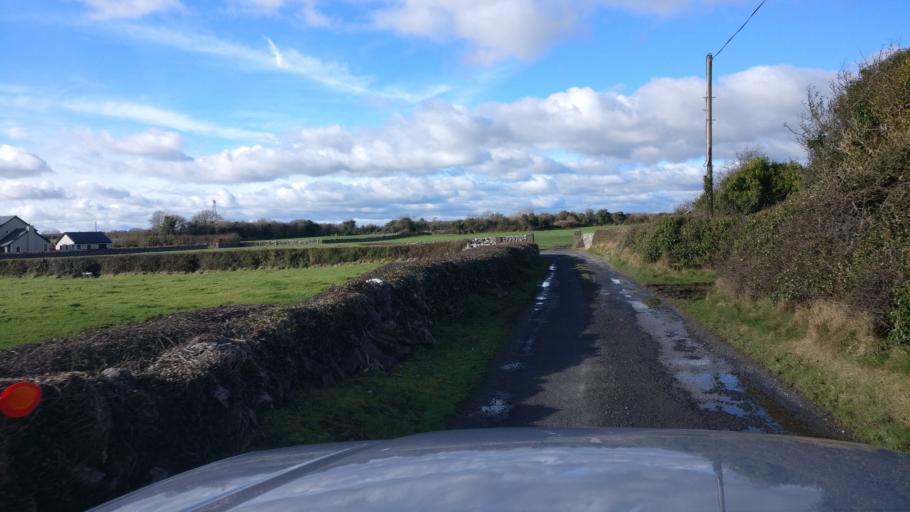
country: IE
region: Connaught
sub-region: County Galway
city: Athenry
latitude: 53.2265
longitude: -8.8112
